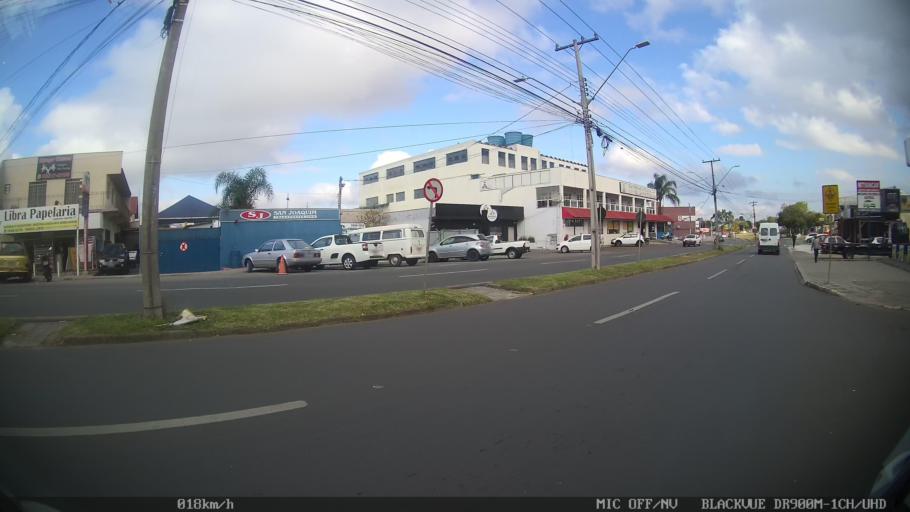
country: BR
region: Parana
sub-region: Pinhais
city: Pinhais
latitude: -25.4043
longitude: -49.1831
